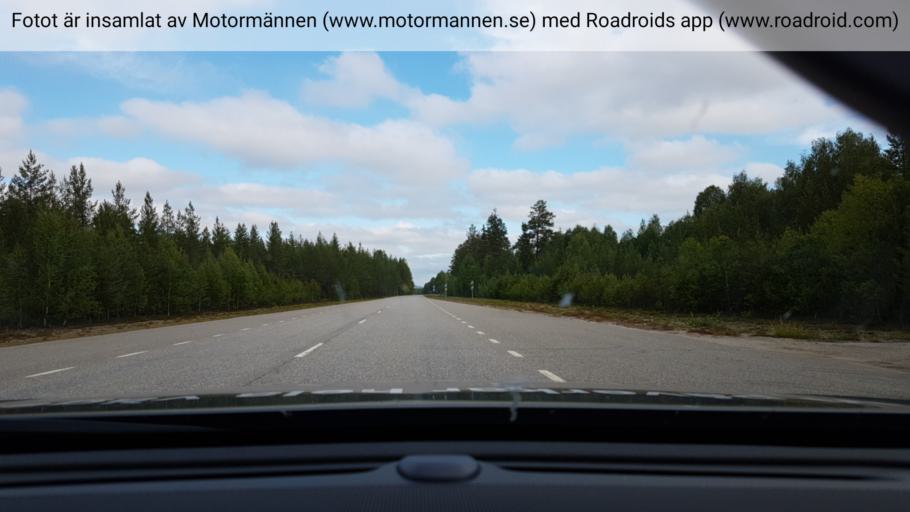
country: SE
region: Vaesterbotten
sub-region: Norsjo Kommun
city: Norsjoe
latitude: 64.5748
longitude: 19.3072
